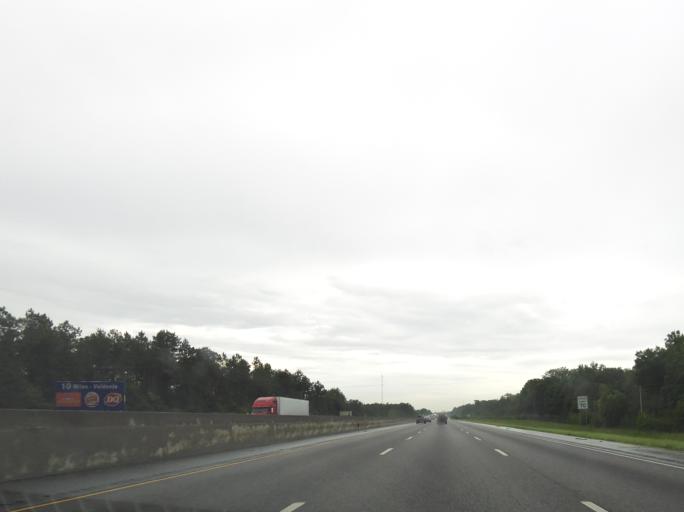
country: US
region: Georgia
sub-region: Lowndes County
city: Hahira
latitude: 31.0273
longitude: -83.3975
